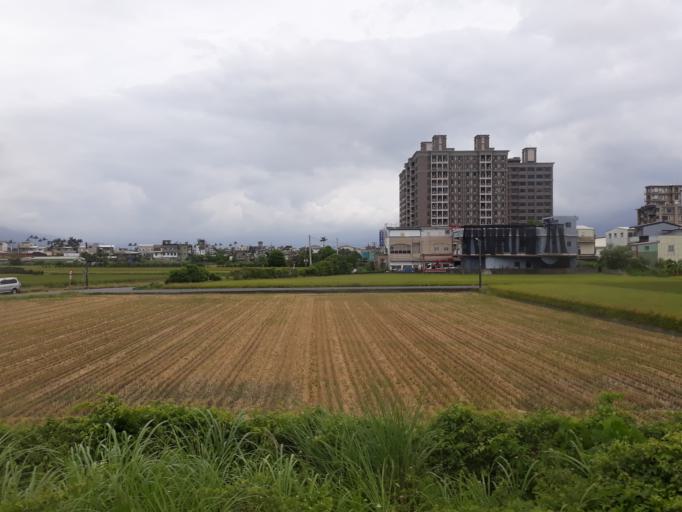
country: TW
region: Taiwan
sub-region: Yilan
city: Yilan
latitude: 24.6898
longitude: 121.7750
